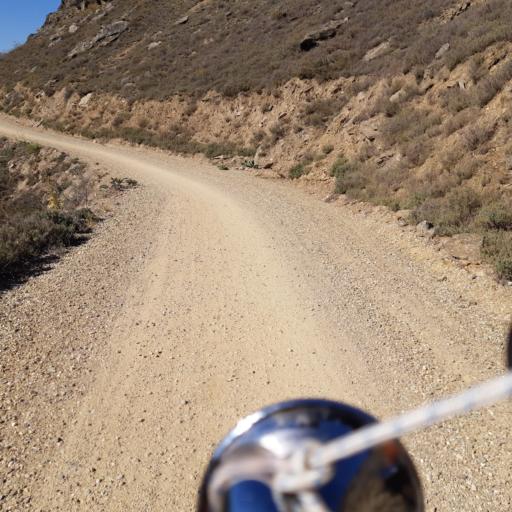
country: NZ
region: Otago
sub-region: Queenstown-Lakes District
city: Wanaka
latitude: -45.0857
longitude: 169.2539
